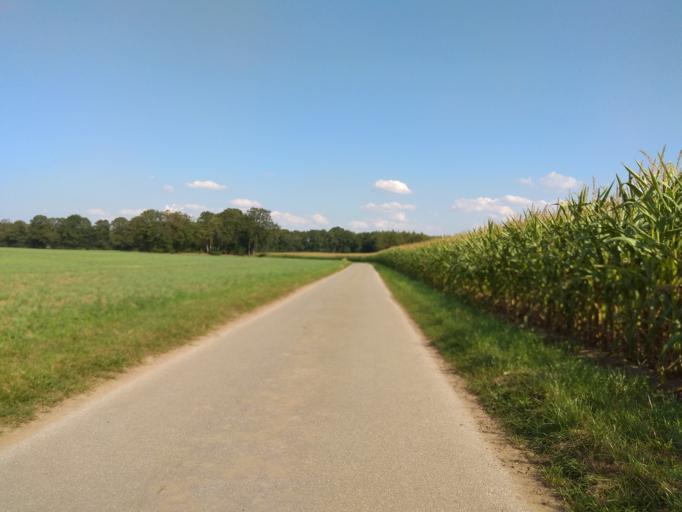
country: DE
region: North Rhine-Westphalia
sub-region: Regierungsbezirk Munster
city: Klein Reken
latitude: 51.7436
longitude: 7.0386
